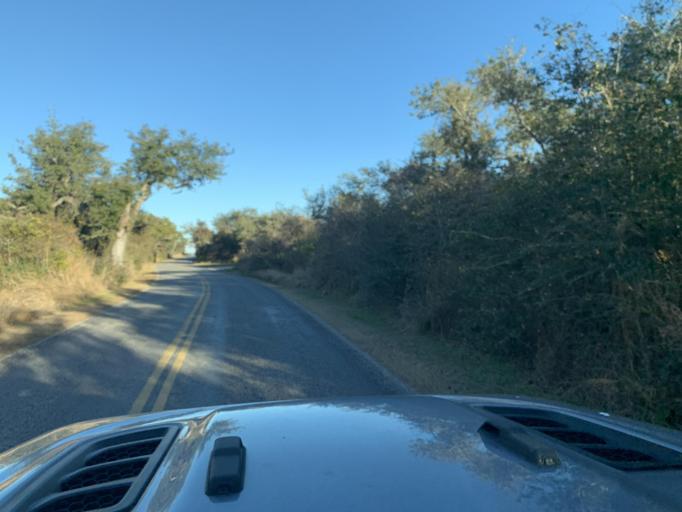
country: US
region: Texas
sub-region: Aransas County
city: Fulton
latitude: 28.1518
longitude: -96.9813
